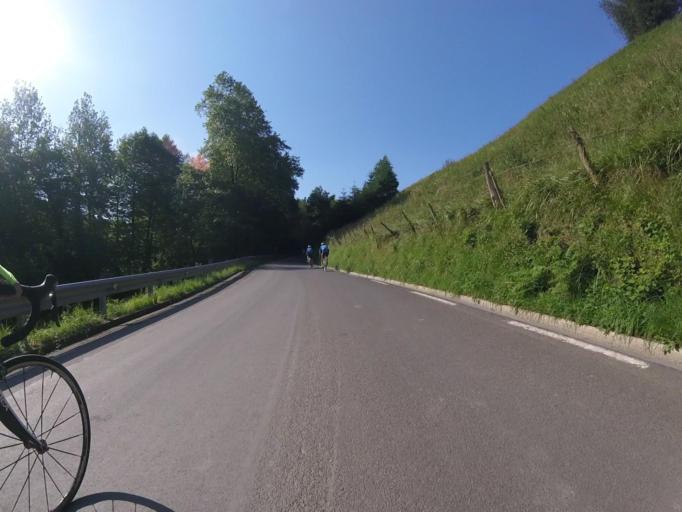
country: ES
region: Basque Country
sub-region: Provincia de Guipuzcoa
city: Zizurkil
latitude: 43.1880
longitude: -2.0825
